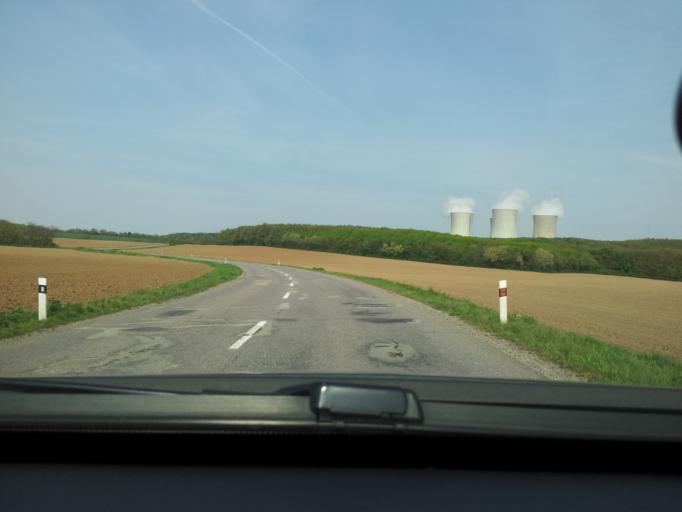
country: SK
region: Nitriansky
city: Tlmace
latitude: 48.2424
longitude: 18.4735
